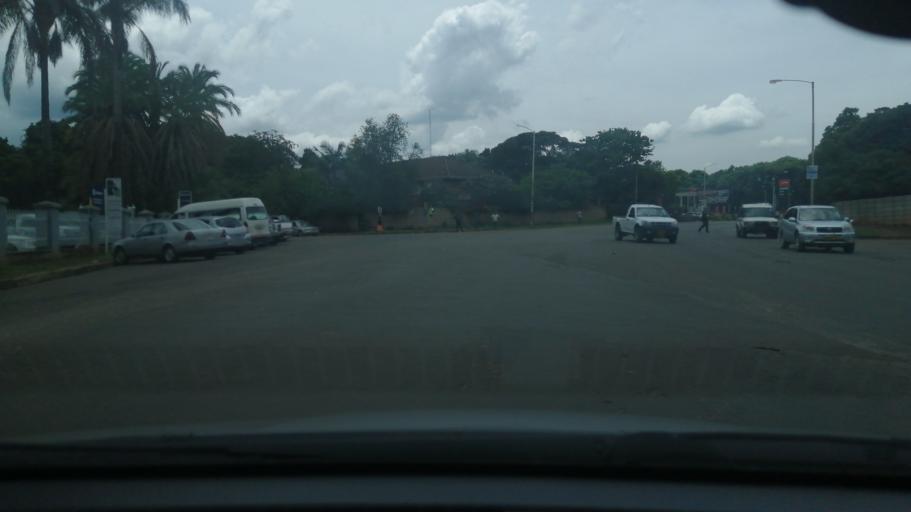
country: ZW
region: Harare
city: Harare
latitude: -17.8056
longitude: 31.0394
